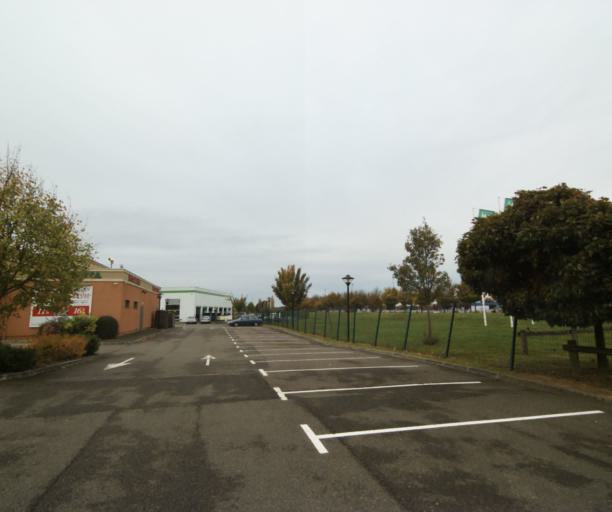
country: FR
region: Centre
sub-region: Departement d'Eure-et-Loir
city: Dreux
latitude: 48.7472
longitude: 1.3452
